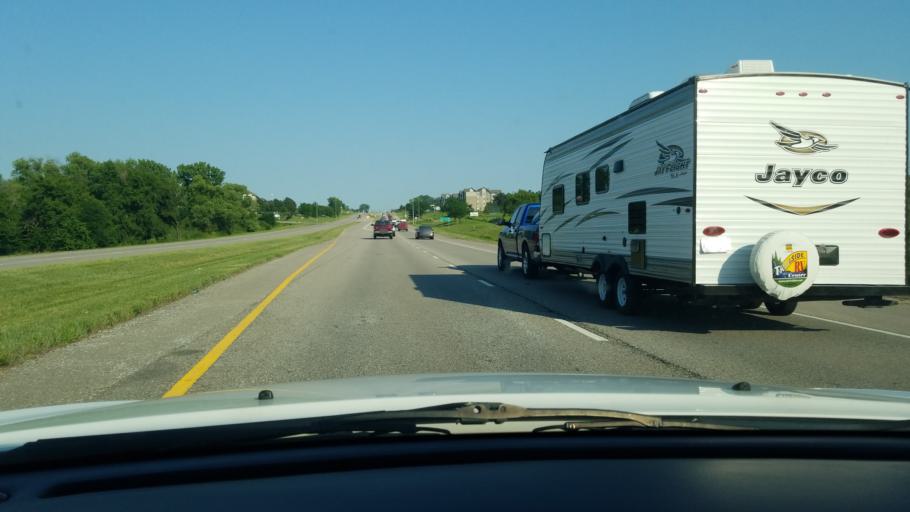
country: US
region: Nebraska
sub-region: Lancaster County
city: Lincoln
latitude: 40.7438
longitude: -96.6211
